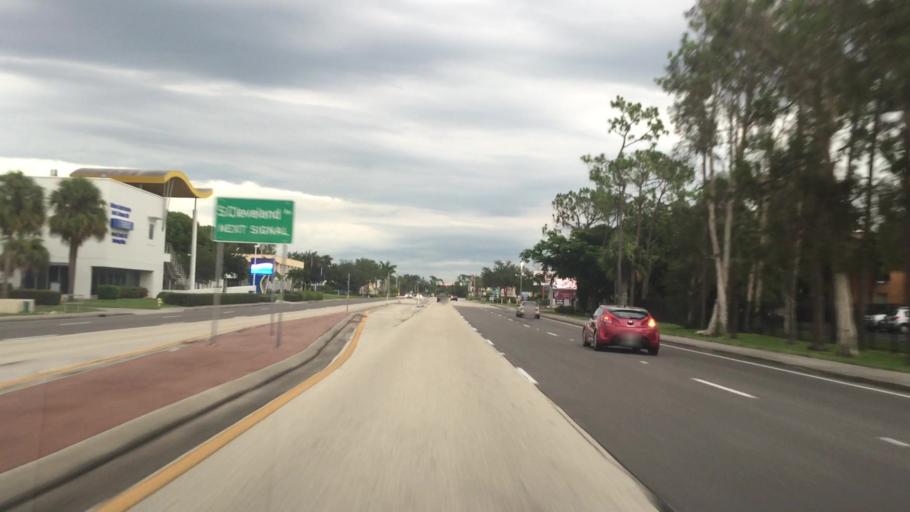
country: US
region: Florida
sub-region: Lee County
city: Villas
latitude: 26.5565
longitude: -81.8761
